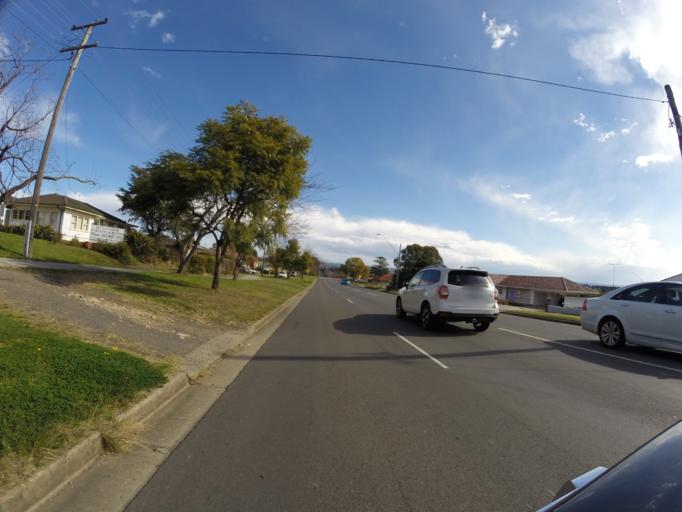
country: AU
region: New South Wales
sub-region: Camden
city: Narellan
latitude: -34.0426
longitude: 150.7294
